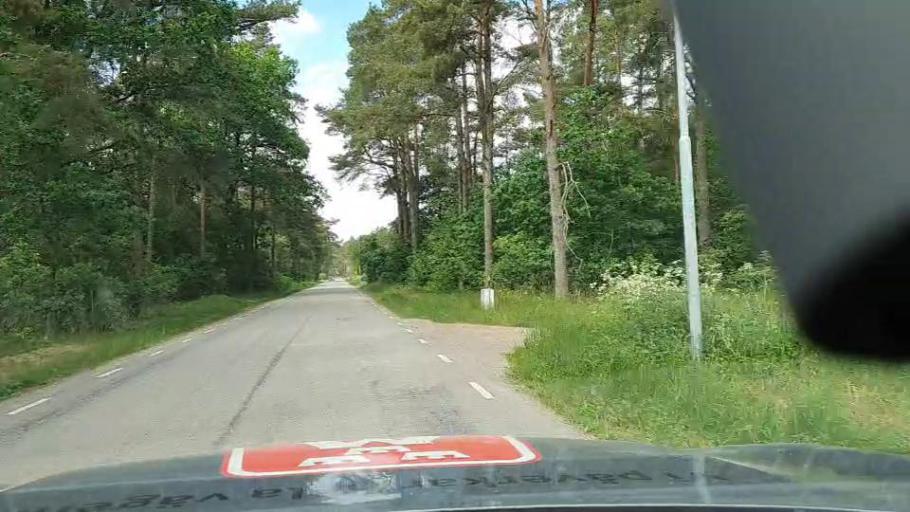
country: SE
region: Blekinge
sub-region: Karlshamns Kommun
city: Morrum
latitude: 56.0935
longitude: 14.6950
